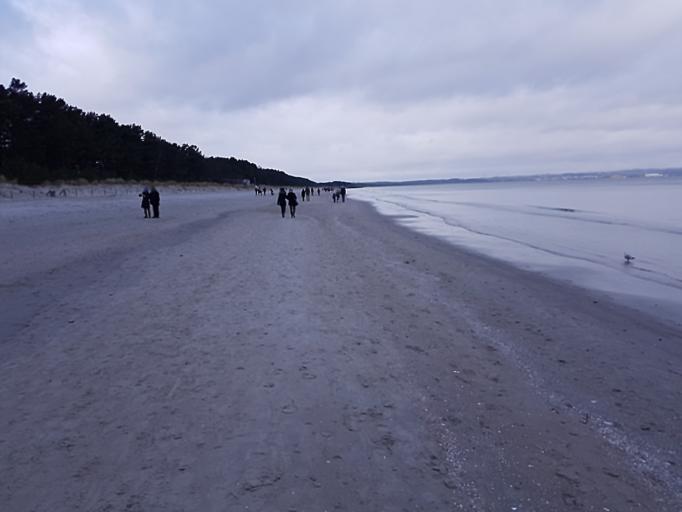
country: DE
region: Mecklenburg-Vorpommern
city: Ostseebad Binz
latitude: 54.4292
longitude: 13.5849
